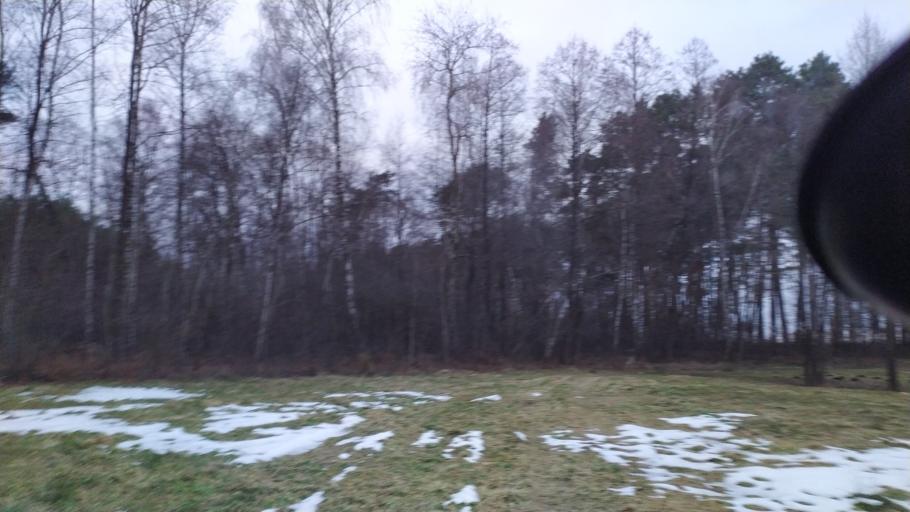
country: PL
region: Lublin Voivodeship
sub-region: Powiat lubartowski
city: Abramow
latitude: 51.4289
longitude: 22.2927
